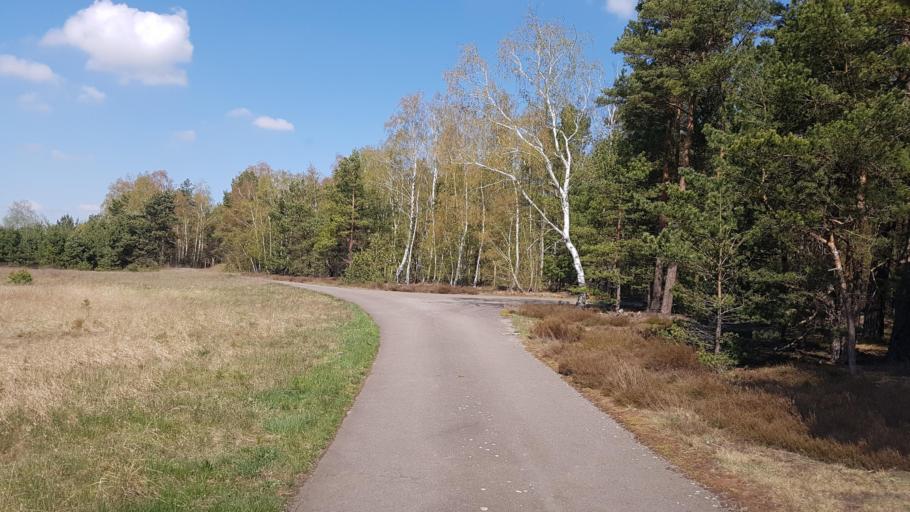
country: DE
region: Brandenburg
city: Bronkow
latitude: 51.6748
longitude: 13.9668
